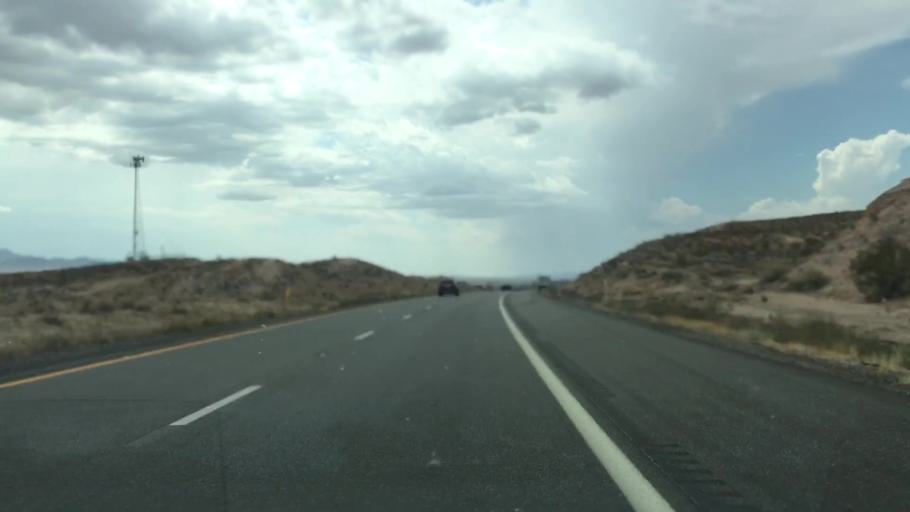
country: US
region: Nevada
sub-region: Clark County
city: Mesquite
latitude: 36.8317
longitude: -114.0070
